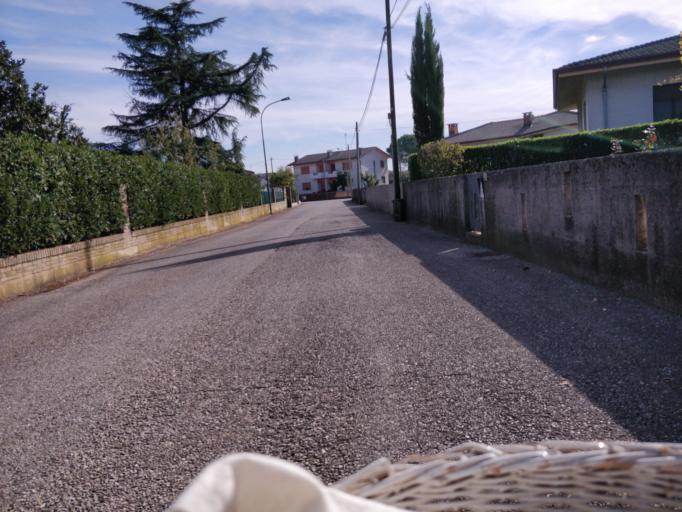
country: IT
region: Friuli Venezia Giulia
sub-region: Provincia di Udine
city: Bertiolo
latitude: 45.9410
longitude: 13.0476
